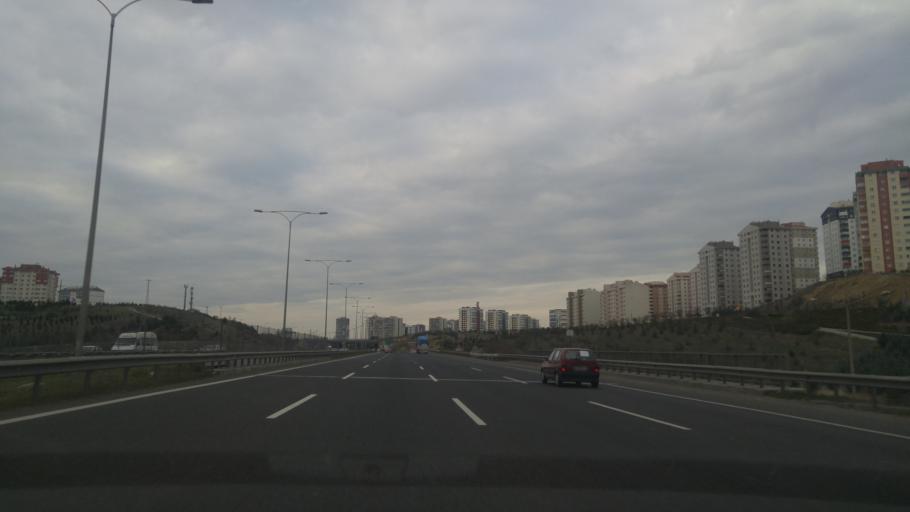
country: TR
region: Ankara
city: Etimesgut
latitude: 39.9913
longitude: 32.6371
